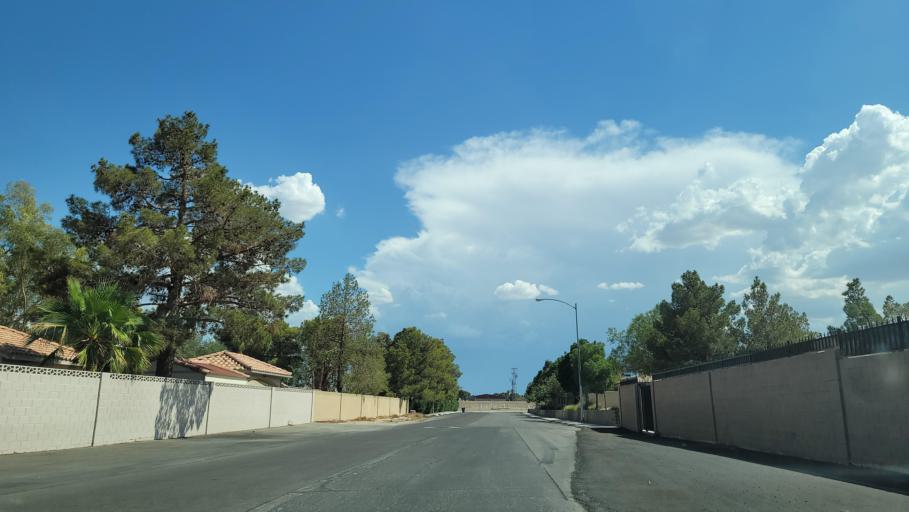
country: US
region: Nevada
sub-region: Clark County
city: Spring Valley
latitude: 36.1310
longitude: -115.2273
